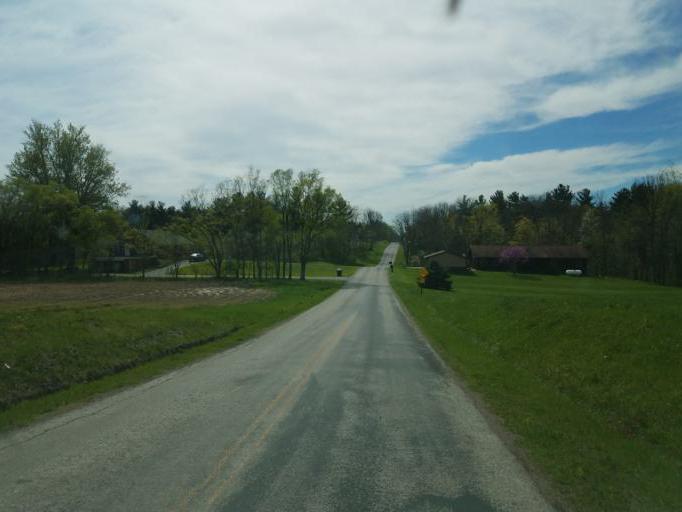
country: US
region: Ohio
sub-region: Richland County
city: Shelby
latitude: 40.9044
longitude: -82.5639
